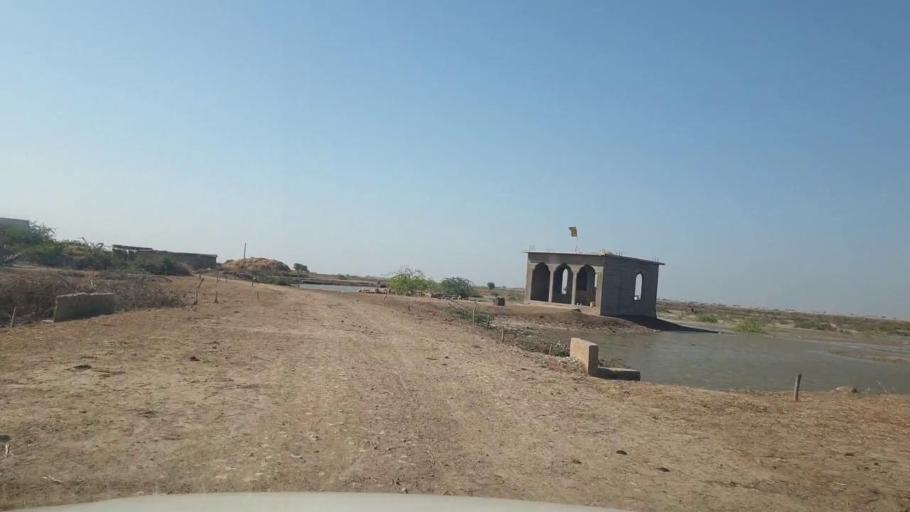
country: PK
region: Sindh
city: Chuhar Jamali
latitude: 24.4385
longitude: 67.8423
